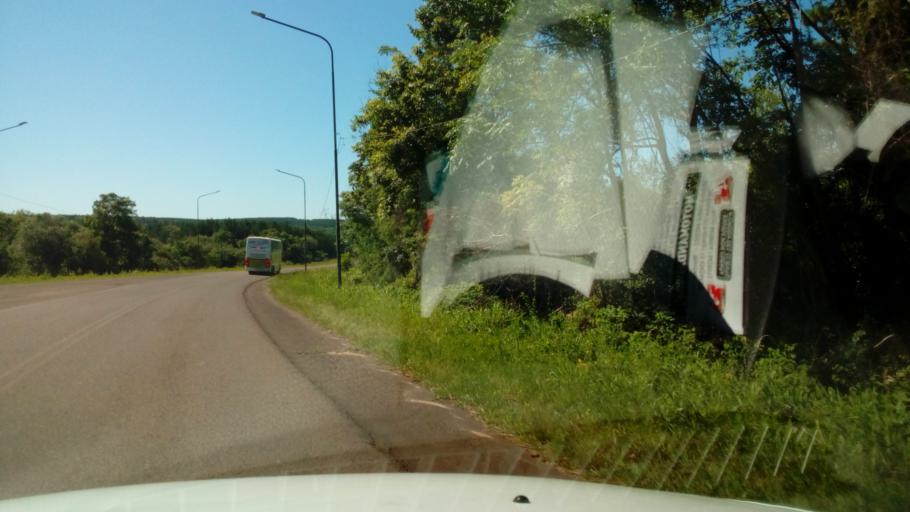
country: AR
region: Misiones
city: Santa Ana
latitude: -27.4156
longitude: -55.5227
